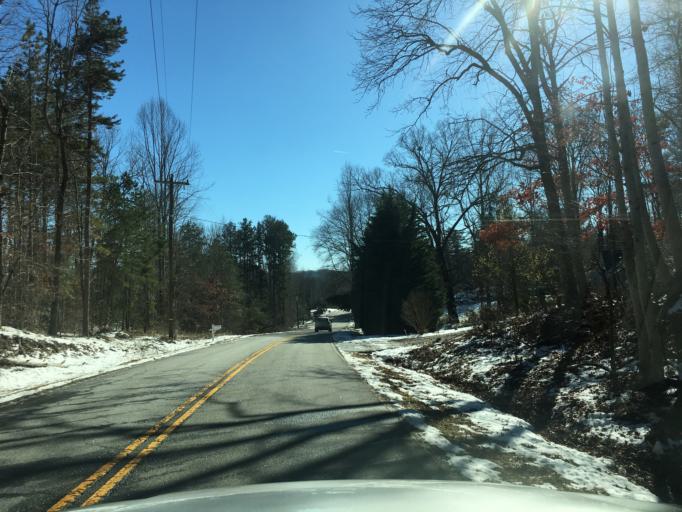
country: US
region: South Carolina
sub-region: Greenville County
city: Slater-Marietta
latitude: 35.0613
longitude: -82.6166
